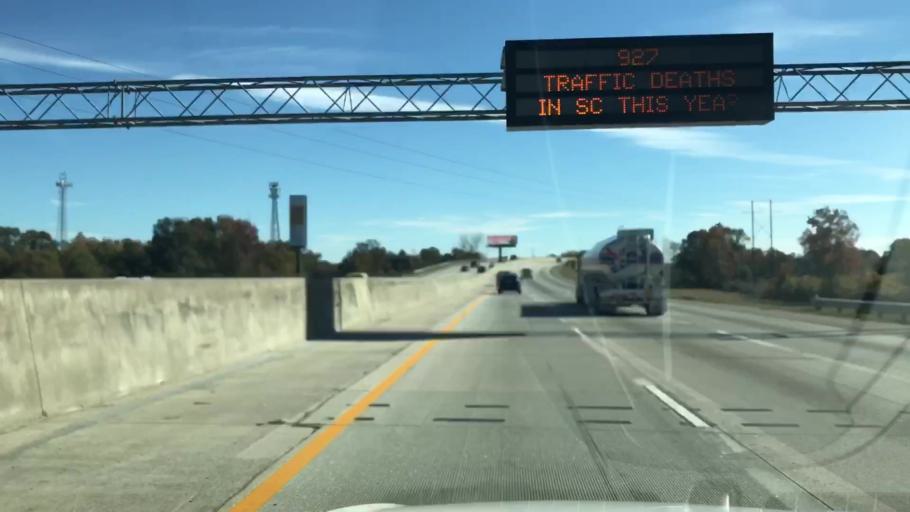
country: US
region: South Carolina
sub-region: Charleston County
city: North Charleston
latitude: 32.8669
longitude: -80.0021
